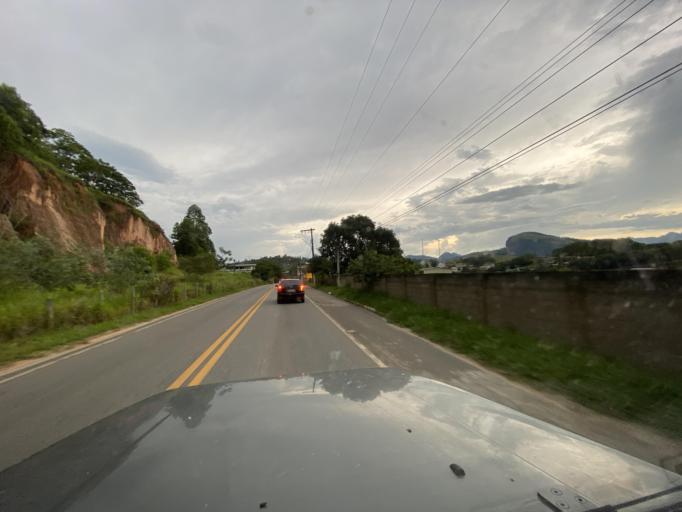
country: BR
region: Espirito Santo
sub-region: Jeronimo Monteiro
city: Jeronimo Monteiro
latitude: -20.7911
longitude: -41.3866
